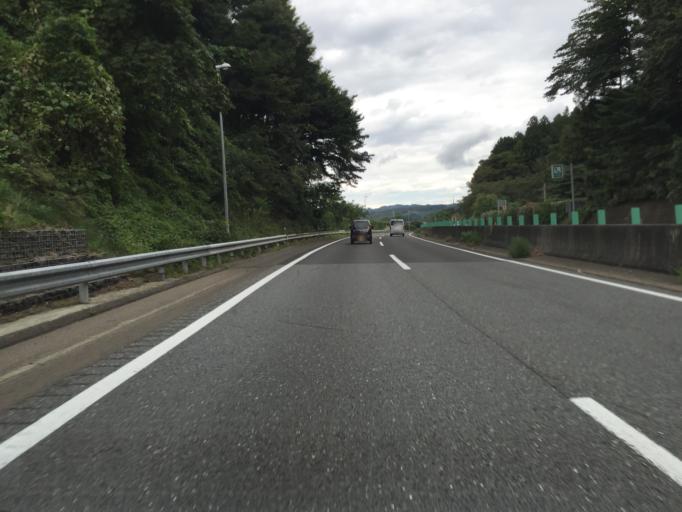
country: JP
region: Miyagi
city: Okawara
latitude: 38.1027
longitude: 140.6888
